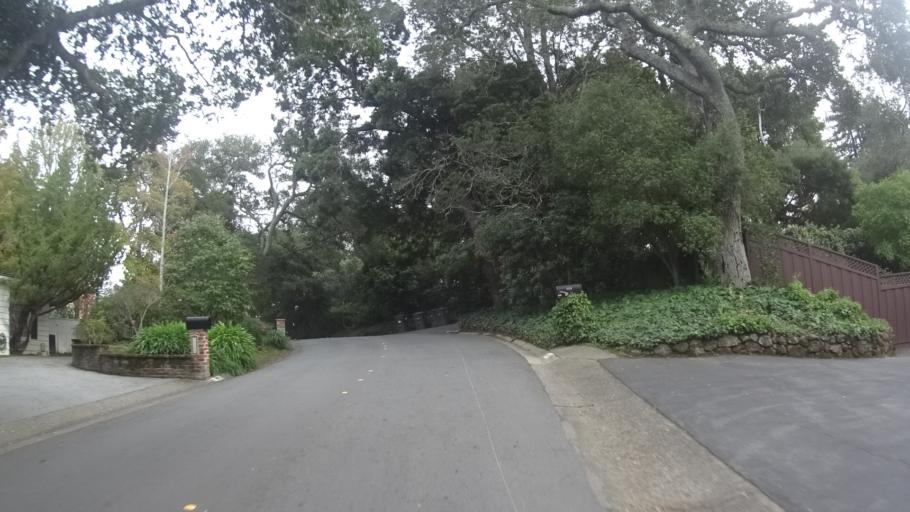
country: US
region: California
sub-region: San Mateo County
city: Hillsborough
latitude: 37.5762
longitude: -122.3712
